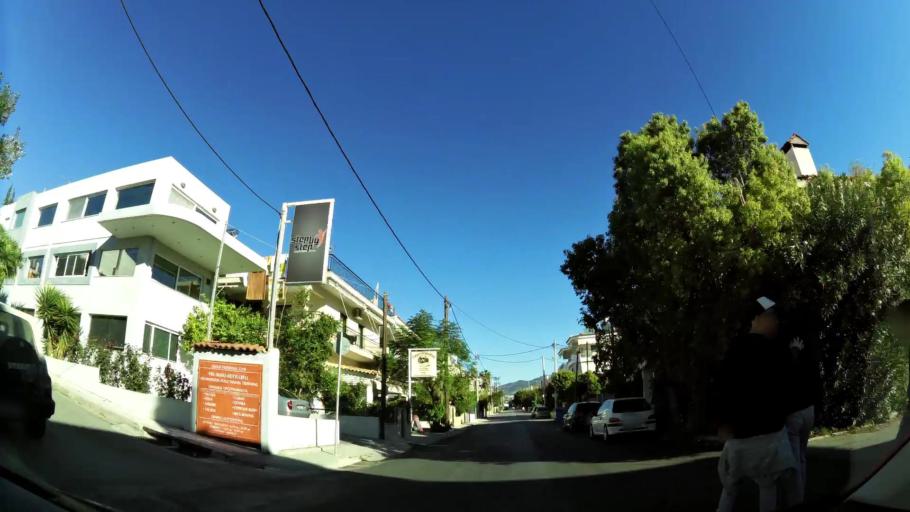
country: GR
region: Attica
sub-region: Nomarchia Anatolikis Attikis
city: Gerakas
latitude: 38.0142
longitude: 23.8496
